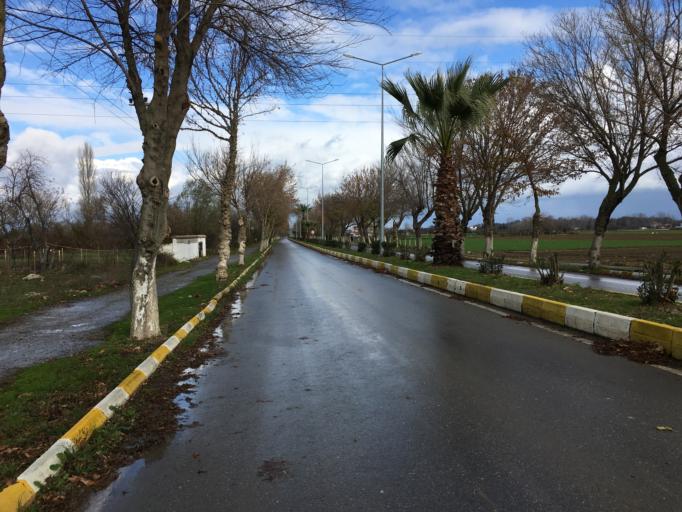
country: TR
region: Samsun
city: Alacam
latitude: 41.6228
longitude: 35.6081
